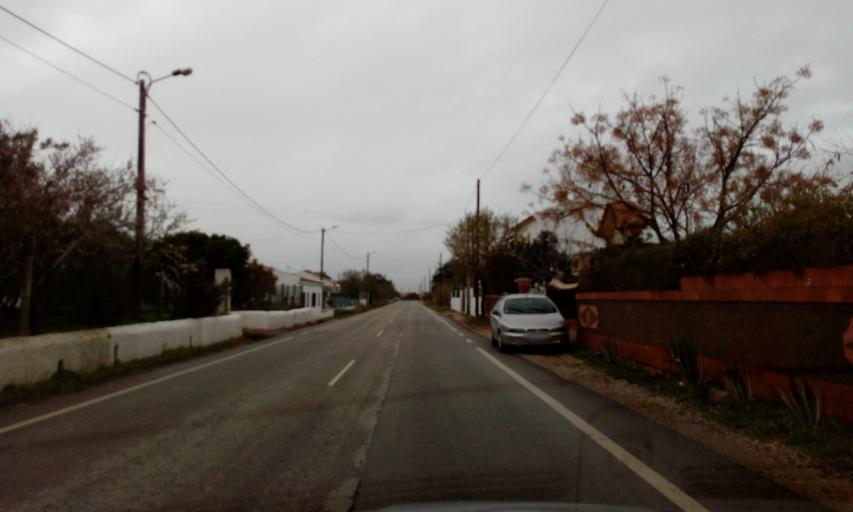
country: PT
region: Faro
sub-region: Albufeira
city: Guia
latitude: 37.1534
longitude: -8.2766
